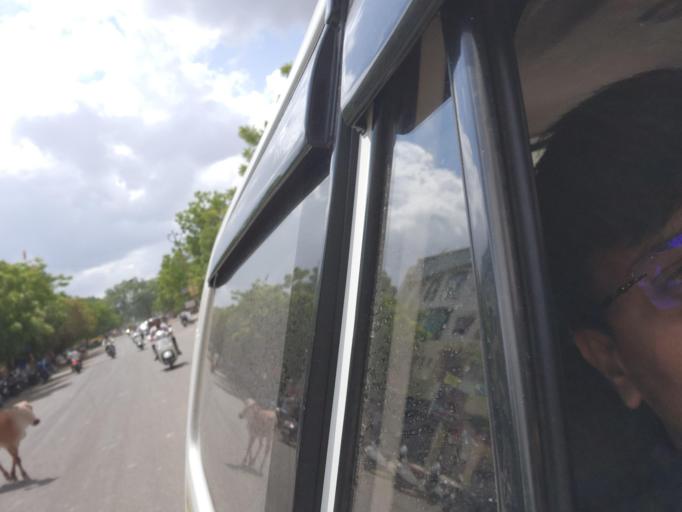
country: IN
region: Gujarat
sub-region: Bhavnagar
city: Bhavnagar
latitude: 21.7553
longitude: 72.1511
